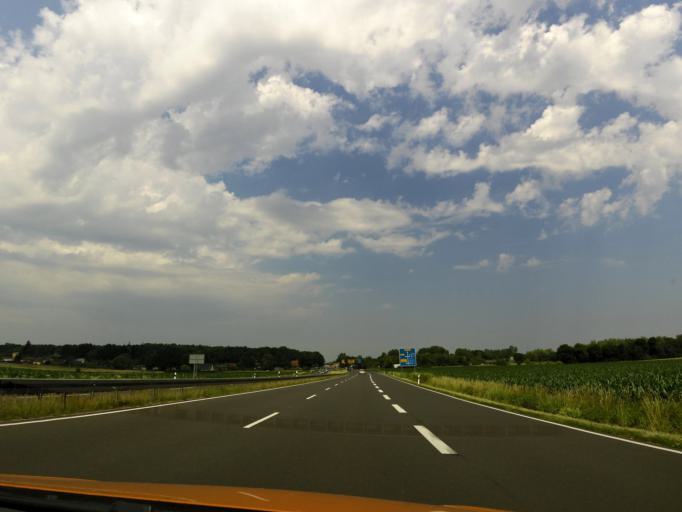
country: DE
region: Brandenburg
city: Wustermark
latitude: 52.4704
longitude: 12.9573
